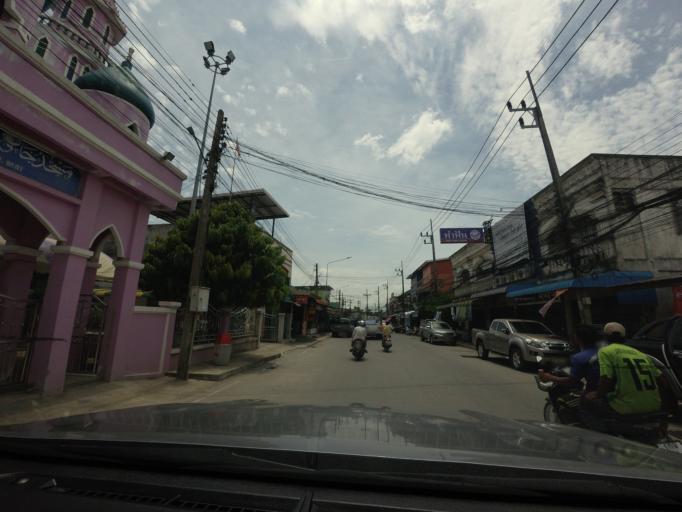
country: TH
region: Yala
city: Yala
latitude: 6.5397
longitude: 101.2932
